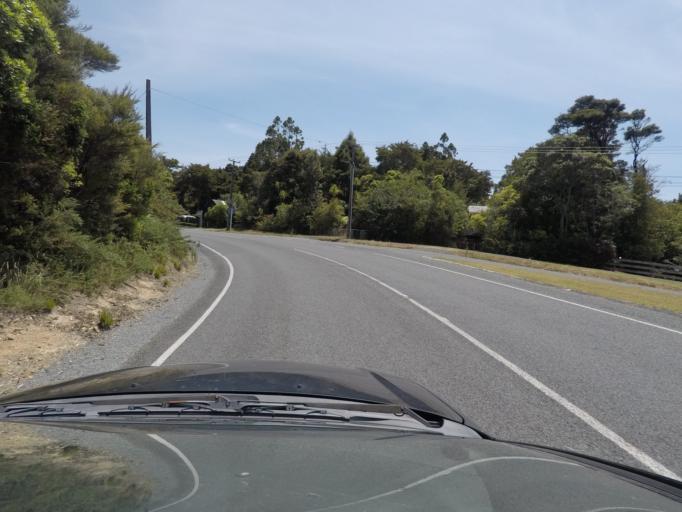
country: NZ
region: Auckland
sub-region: Auckland
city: Warkworth
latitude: -36.2985
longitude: 174.7951
